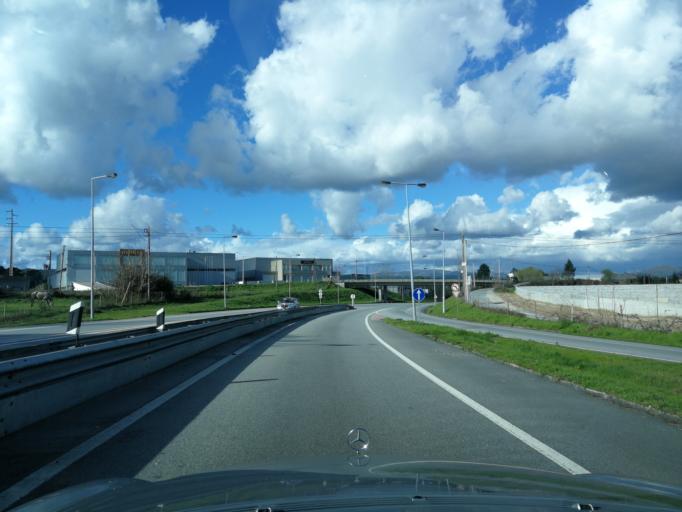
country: PT
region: Braga
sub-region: Vila Verde
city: Prado
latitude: 41.6075
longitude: -8.4590
